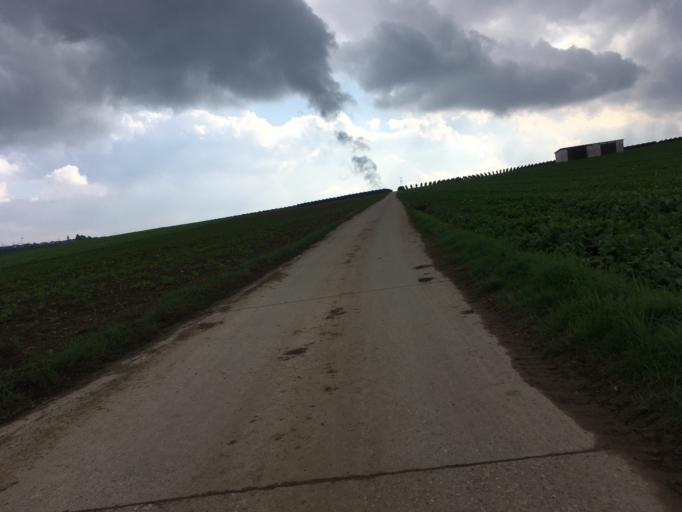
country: DE
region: Baden-Wuerttemberg
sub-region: Regierungsbezirk Stuttgart
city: Lauffen am Neckar
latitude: 49.0622
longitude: 9.1677
